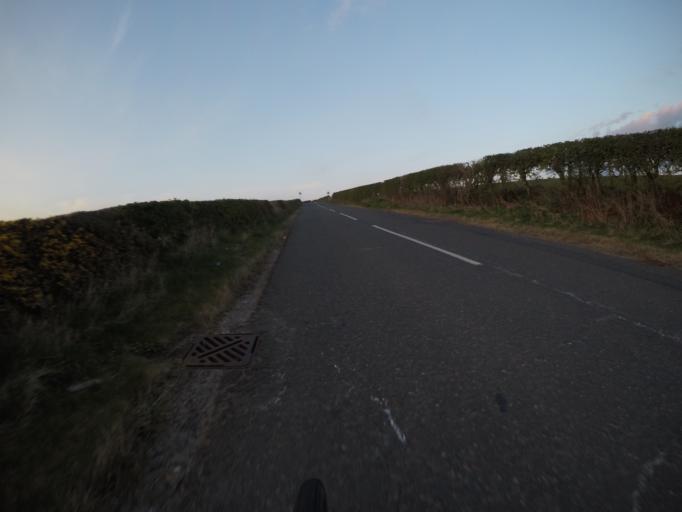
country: GB
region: Scotland
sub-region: South Ayrshire
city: Dundonald
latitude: 55.5567
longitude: -4.6151
